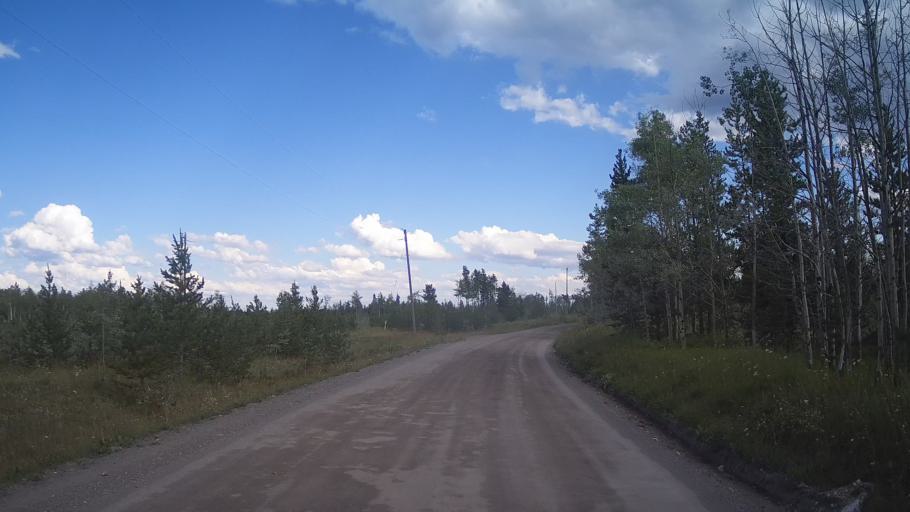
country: CA
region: British Columbia
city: Cache Creek
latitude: 51.2539
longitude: -121.6758
